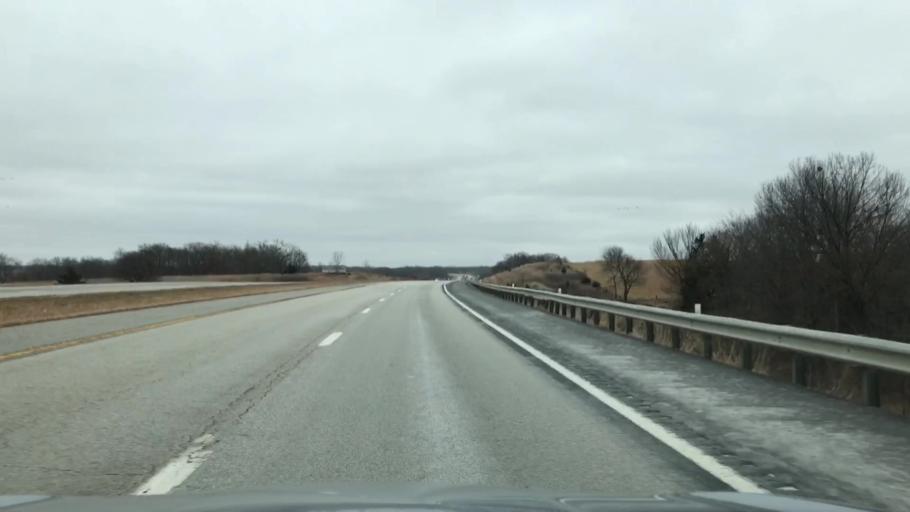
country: US
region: Missouri
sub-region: Caldwell County
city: Hamilton
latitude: 39.7467
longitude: -94.0479
